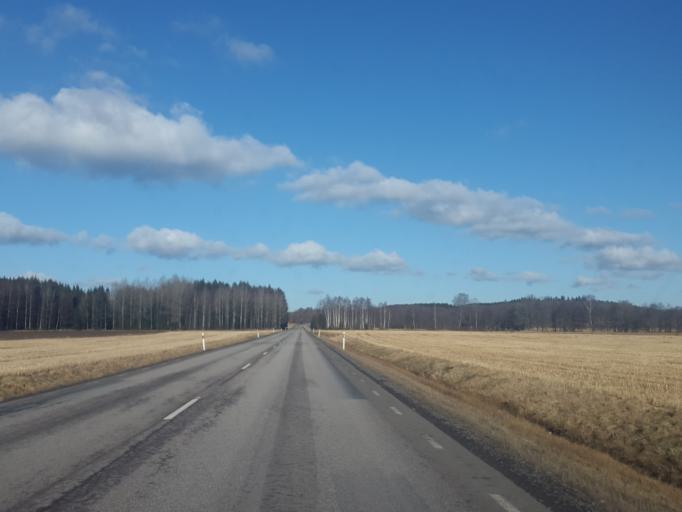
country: SE
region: Vaestra Goetaland
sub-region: Lerums Kommun
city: Grabo
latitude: 57.9098
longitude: 12.3404
